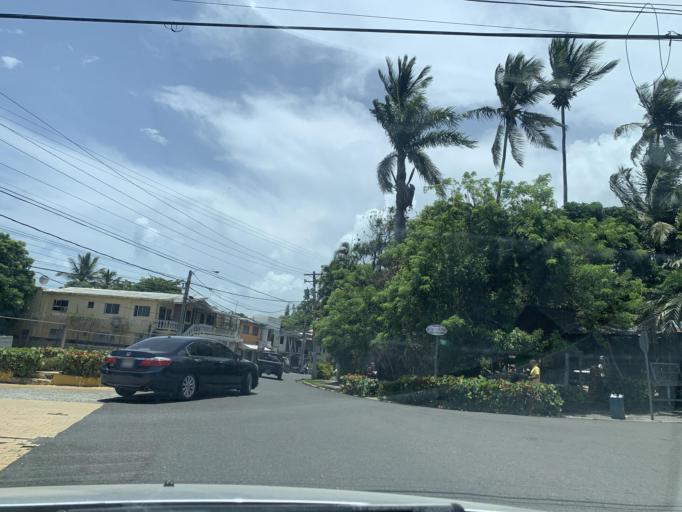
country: DO
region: Puerto Plata
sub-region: Puerto Plata
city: Puerto Plata
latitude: 19.7939
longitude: -70.6843
